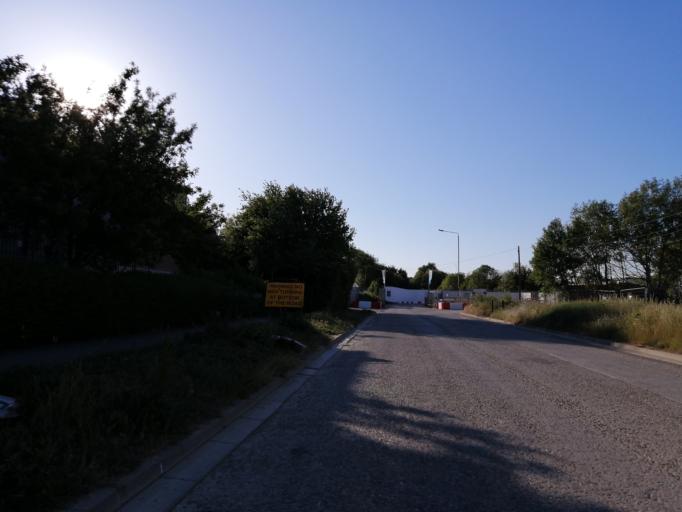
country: GB
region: England
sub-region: Peterborough
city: Marholm
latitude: 52.6077
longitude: -0.2848
